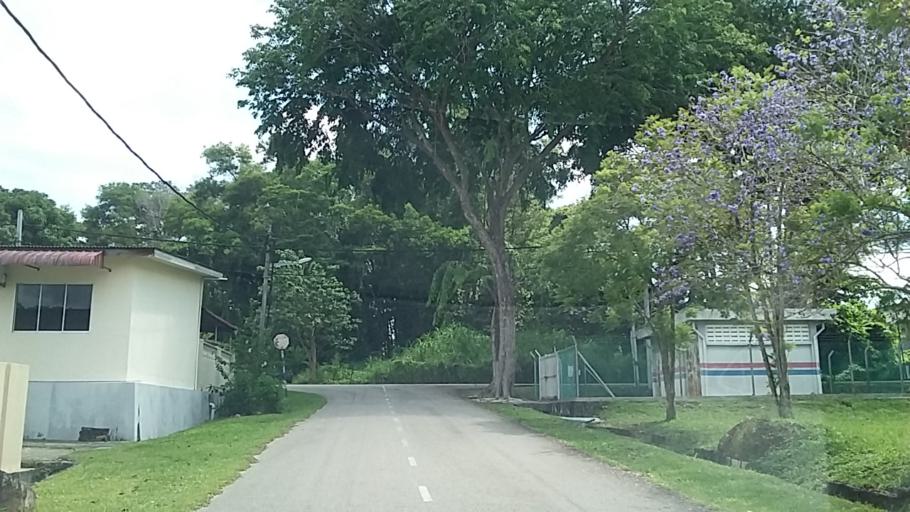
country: MY
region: Johor
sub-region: Daerah Batu Pahat
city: Batu Pahat
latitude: 1.8435
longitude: 102.9483
